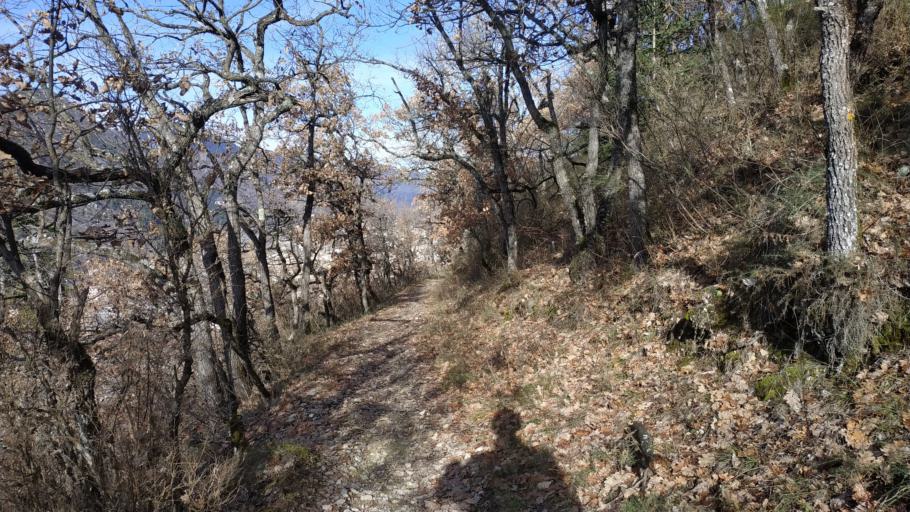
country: FR
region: Provence-Alpes-Cote d'Azur
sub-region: Departement des Alpes-de-Haute-Provence
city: Digne-les-Bains
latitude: 44.0849
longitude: 6.2324
